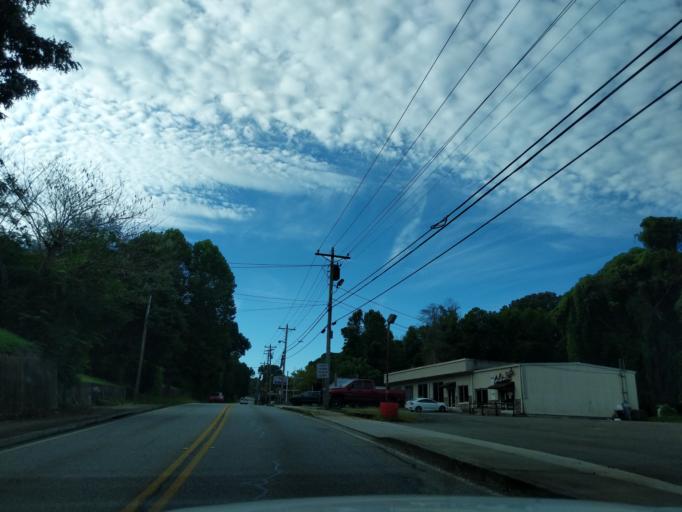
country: US
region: Georgia
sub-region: Fannin County
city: McCaysville
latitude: 34.9826
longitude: -84.3746
